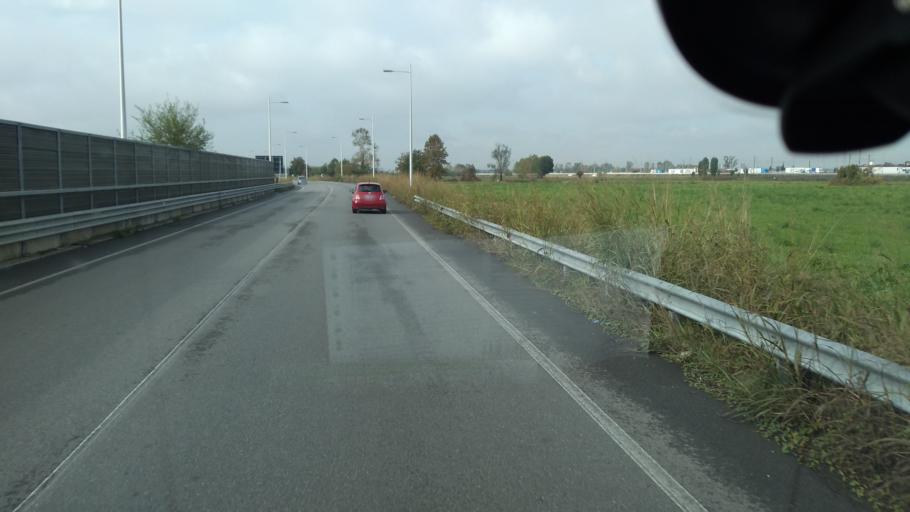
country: IT
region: Lombardy
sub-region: Provincia di Bergamo
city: Caravaggio
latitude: 45.5079
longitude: 9.6400
